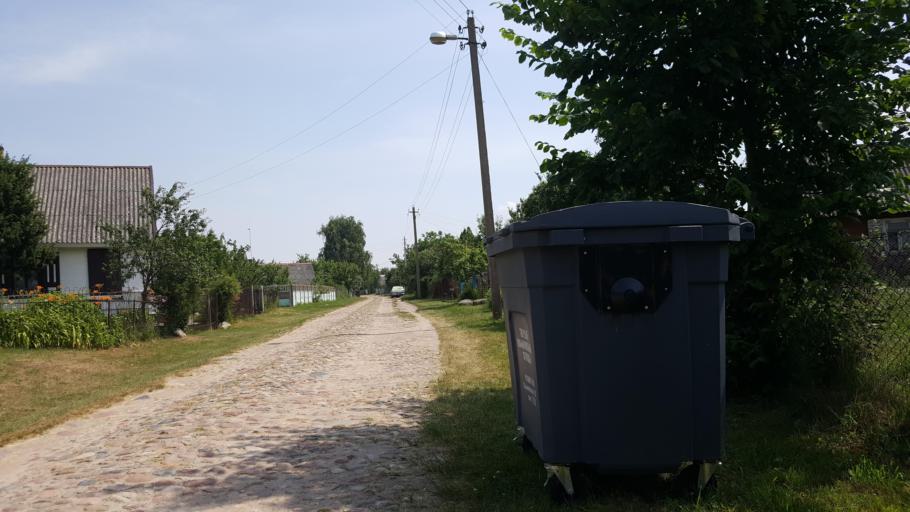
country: BY
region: Brest
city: Kamyanyets
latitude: 52.3571
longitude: 23.7493
